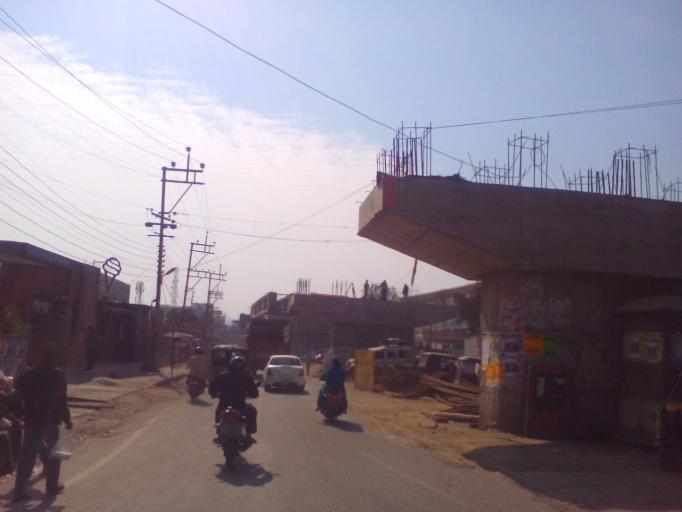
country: IN
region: Uttarakhand
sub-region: Dehradun
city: Clement Town
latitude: 30.2885
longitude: 77.9967
